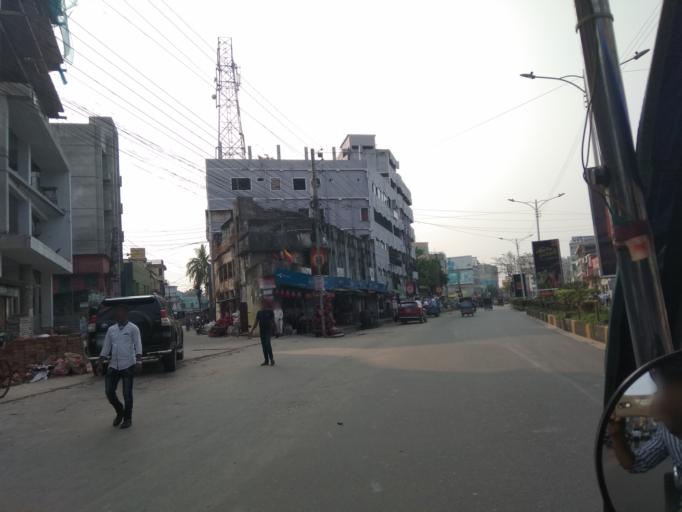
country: BD
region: Khulna
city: Khulna
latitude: 22.8134
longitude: 89.5563
